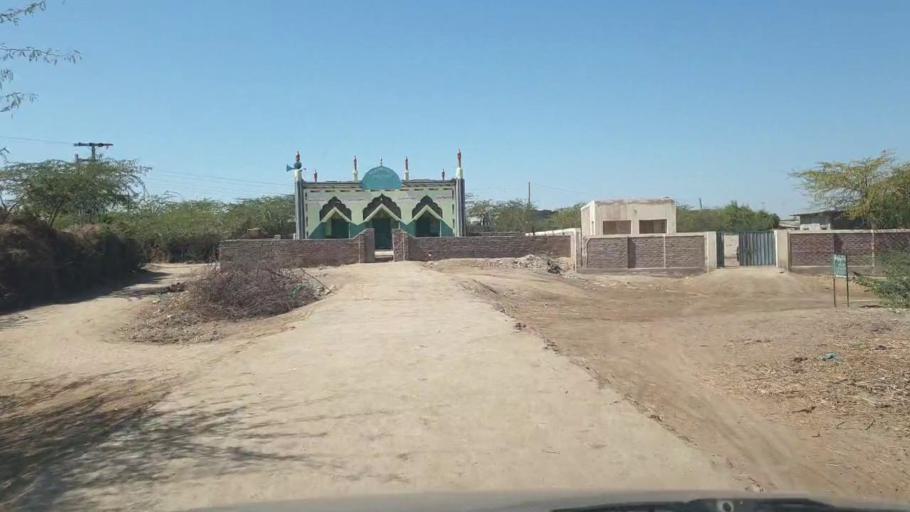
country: PK
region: Sindh
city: Umarkot
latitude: 25.4081
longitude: 69.6360
